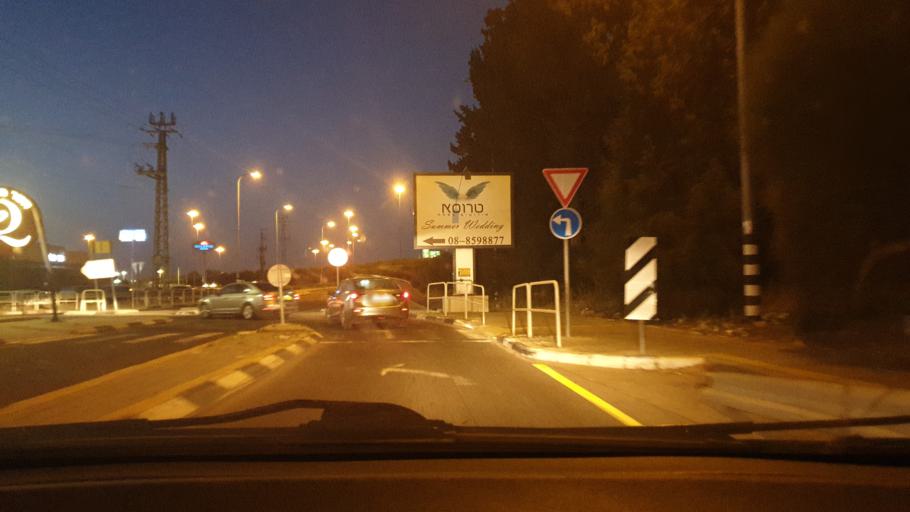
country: IL
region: Central District
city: Bene 'Ayish
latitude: 31.7993
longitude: 34.7620
